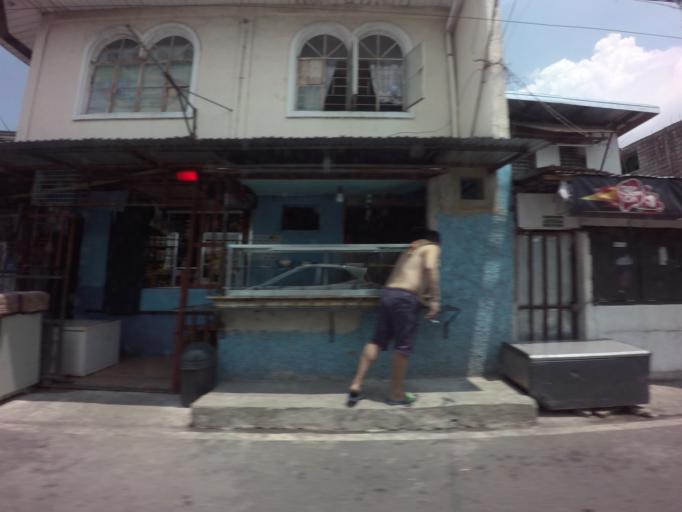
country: PH
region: Calabarzon
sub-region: Province of Laguna
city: San Pedro
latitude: 14.4108
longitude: 121.0500
